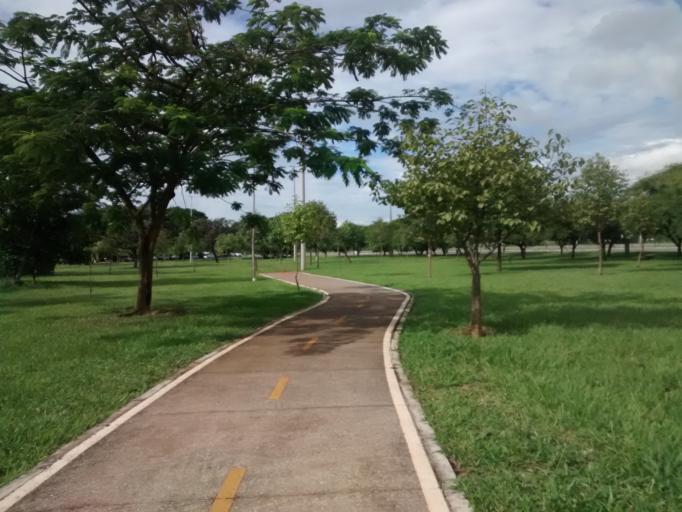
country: BR
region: Federal District
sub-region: Brasilia
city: Brasilia
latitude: -15.7990
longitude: -47.9153
